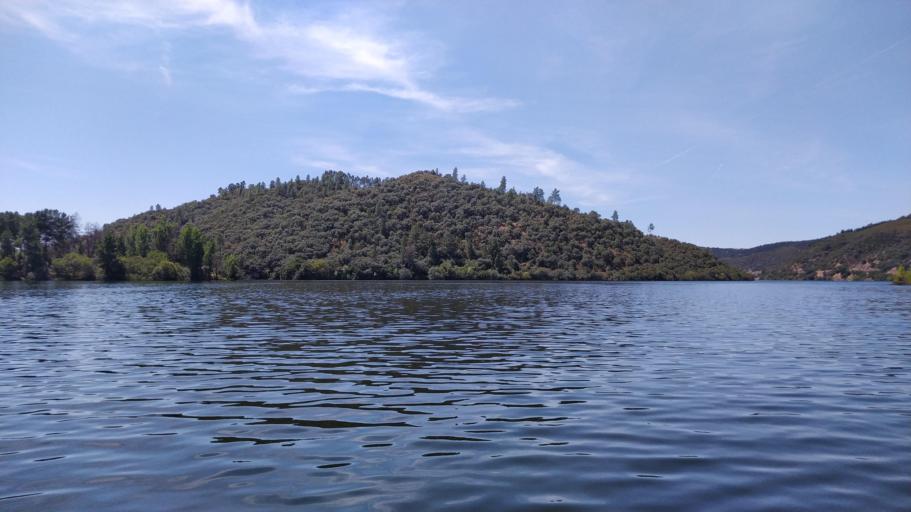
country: PT
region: Portalegre
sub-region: Nisa
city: Nisa
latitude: 39.6397
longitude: -7.6983
